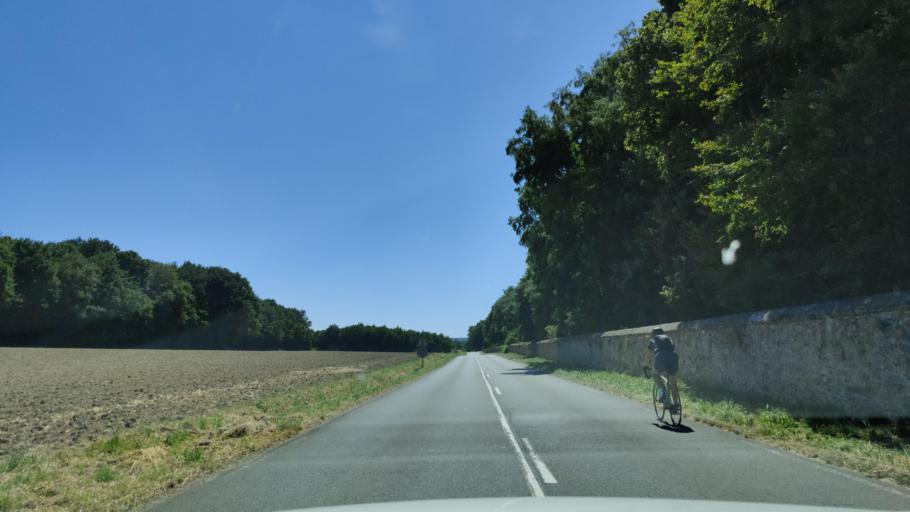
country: FR
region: Ile-de-France
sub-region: Departement de l'Essonne
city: Fontenay-les-Briis
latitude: 48.6063
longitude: 2.1677
